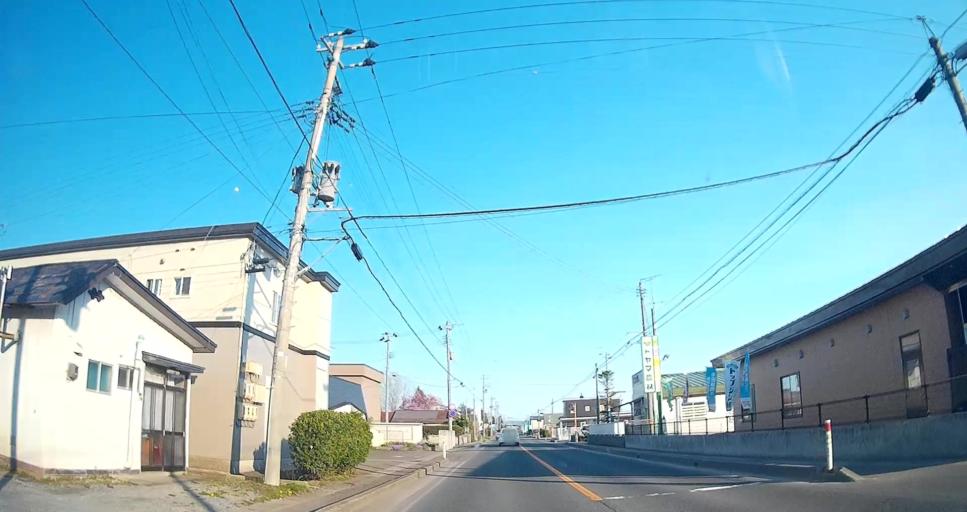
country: JP
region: Aomori
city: Mutsu
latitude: 41.2771
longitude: 141.2123
